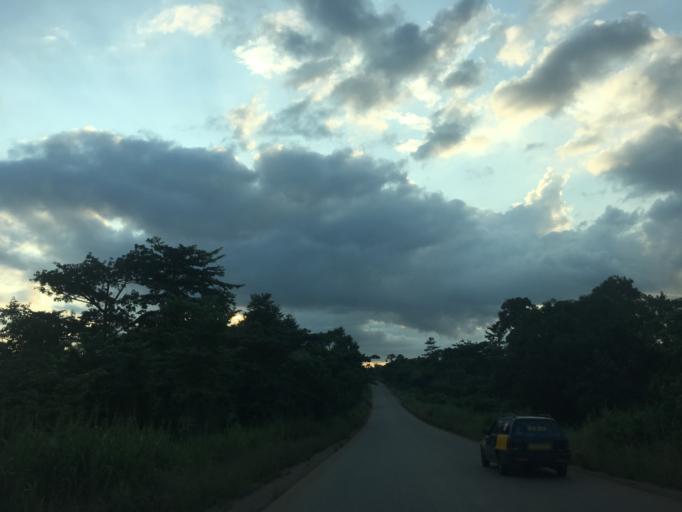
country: GH
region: Western
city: Bibiani
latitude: 6.7138
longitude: -2.4580
